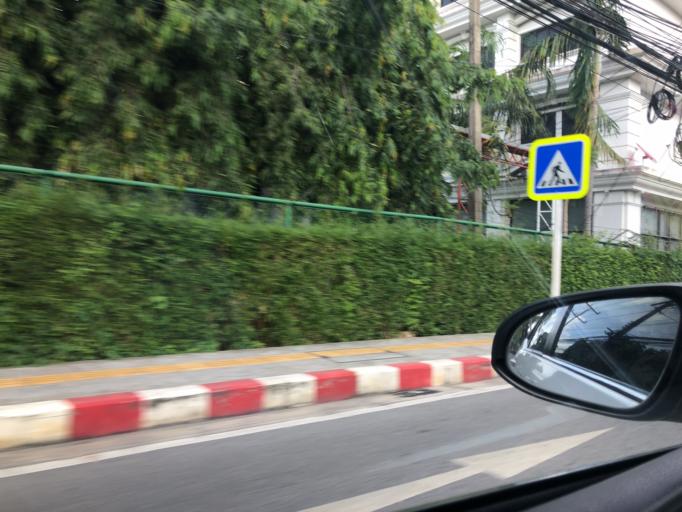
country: TH
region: Phuket
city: Wichit
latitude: 7.8923
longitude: 98.3898
